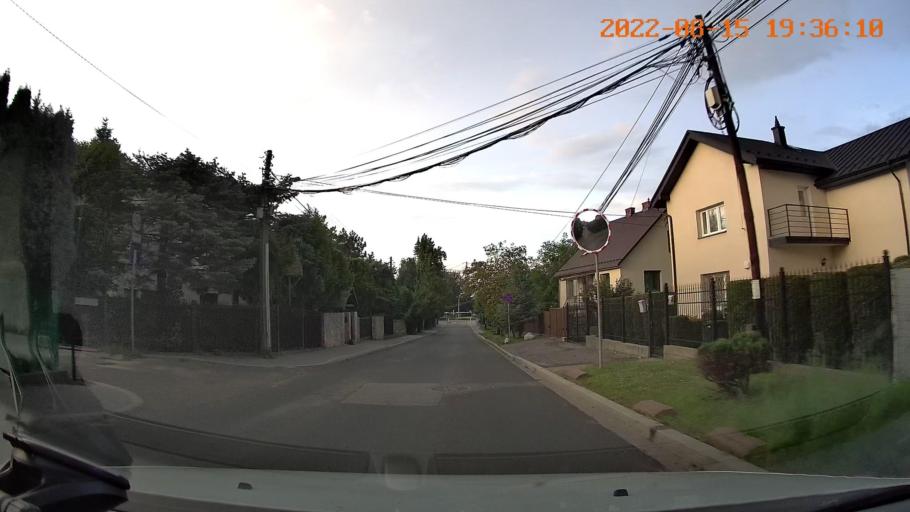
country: PL
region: Lesser Poland Voivodeship
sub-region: Powiat krakowski
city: Rzaska
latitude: 50.0666
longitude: 19.8455
